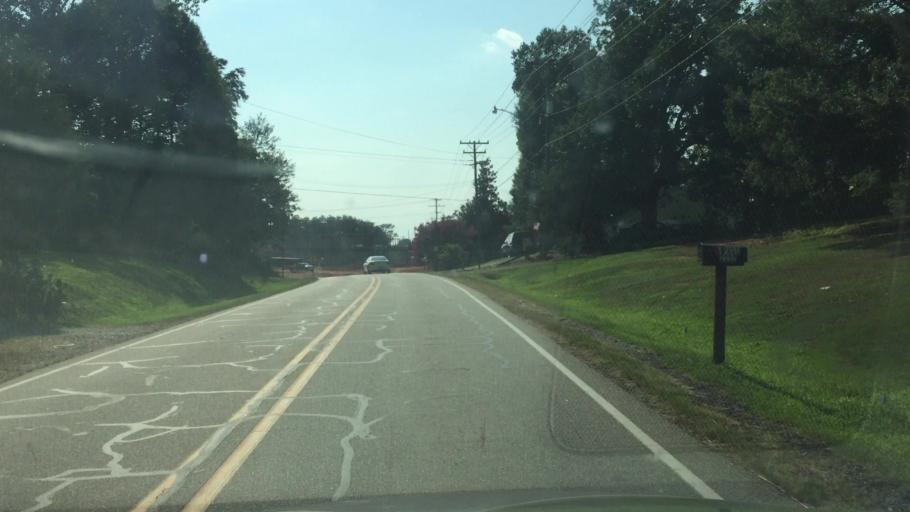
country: US
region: North Carolina
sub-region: Rockingham County
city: Reidsville
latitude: 36.3263
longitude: -79.6378
